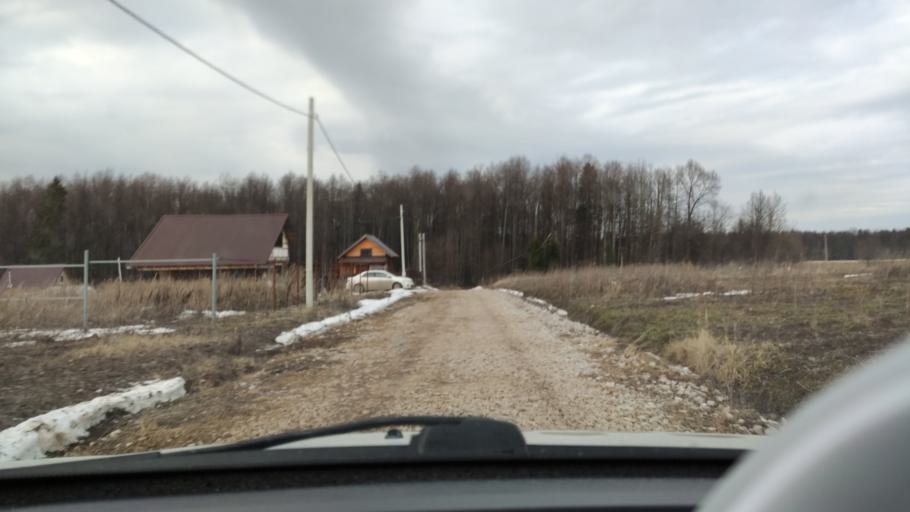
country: RU
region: Perm
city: Ferma
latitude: 57.8832
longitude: 56.3385
